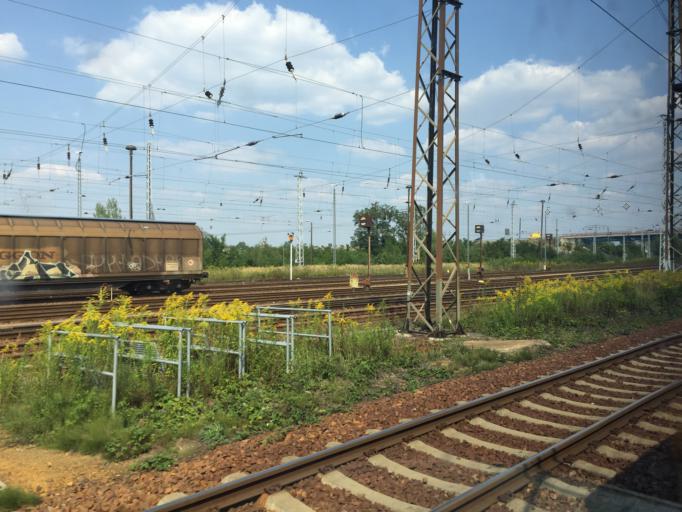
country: DE
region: Brandenburg
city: Senftenberg
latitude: 51.5310
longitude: 14.0117
